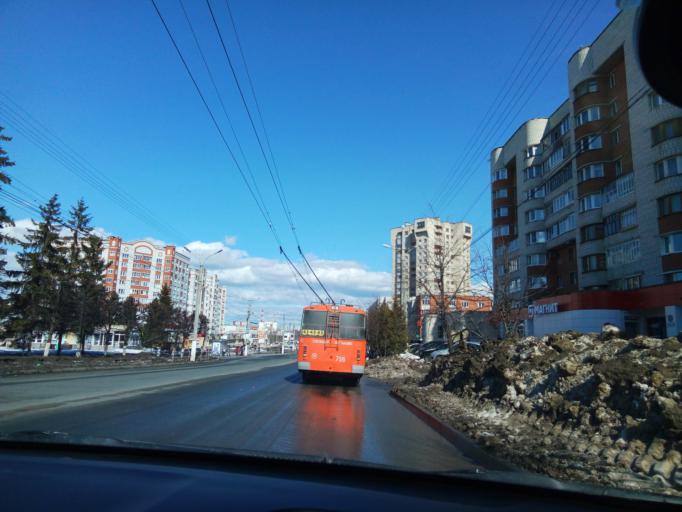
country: RU
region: Chuvashia
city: Novyye Lapsary
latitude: 56.1171
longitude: 47.1824
